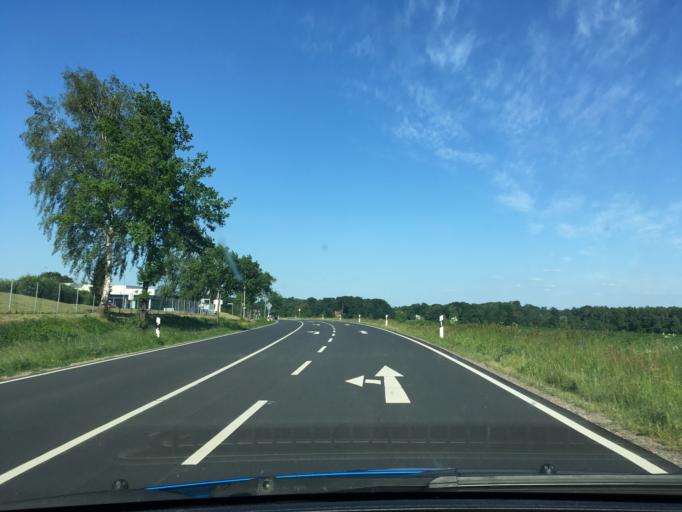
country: DE
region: Lower Saxony
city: Walsrode
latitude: 52.8611
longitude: 9.6183
